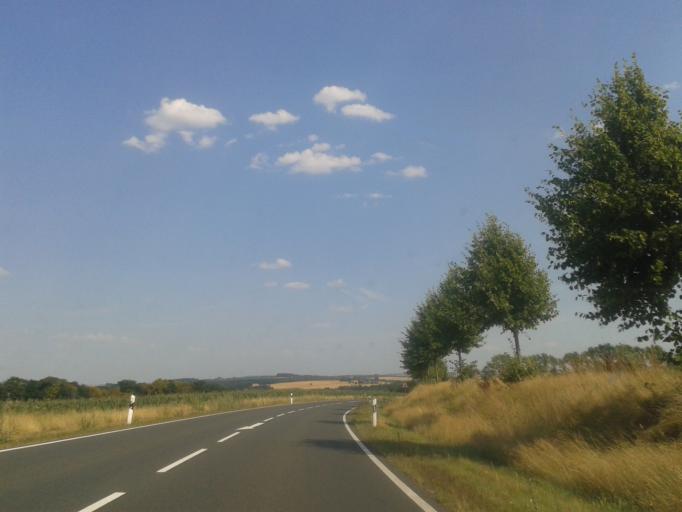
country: DE
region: Saxony
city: Nossen
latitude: 51.0256
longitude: 13.3226
